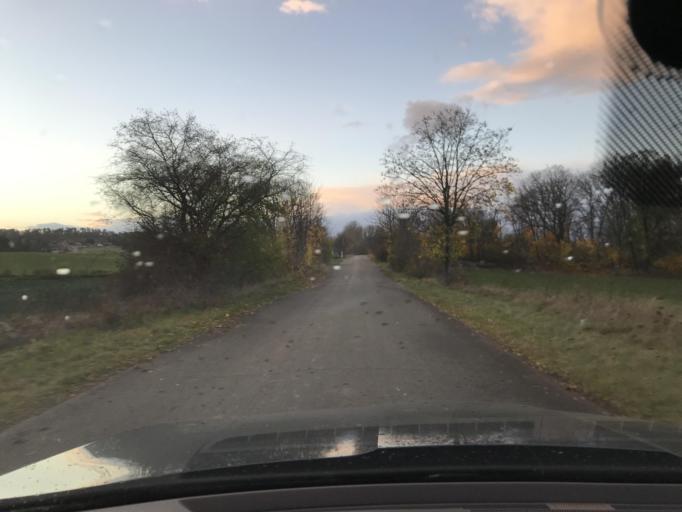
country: DE
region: Saxony-Anhalt
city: Langenstein
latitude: 51.8464
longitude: 11.0157
